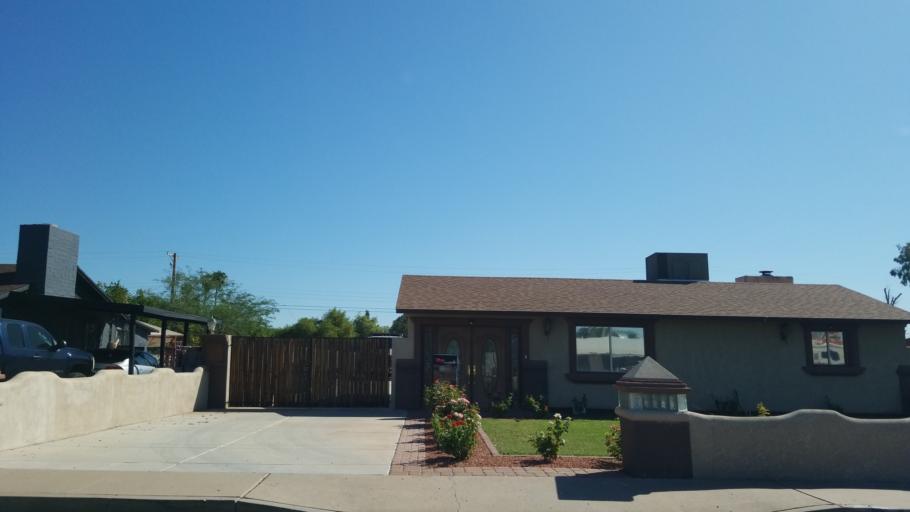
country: US
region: Arizona
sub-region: Maricopa County
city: Glendale
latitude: 33.4826
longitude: -112.1595
